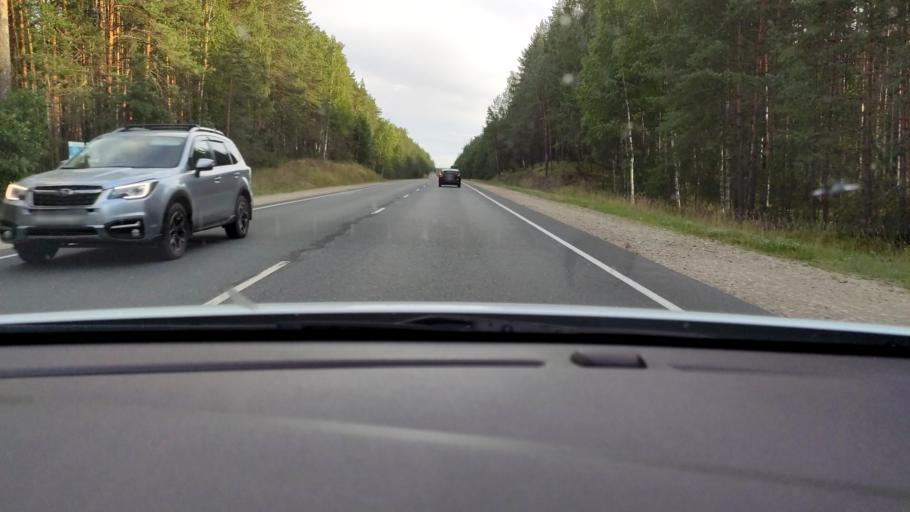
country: RU
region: Mariy-El
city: Pomary
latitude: 56.0430
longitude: 48.3774
